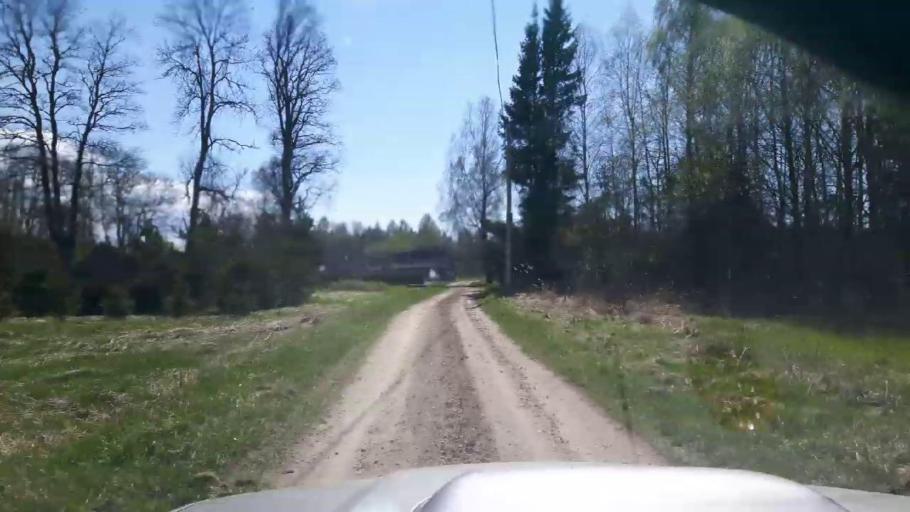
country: EE
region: Paernumaa
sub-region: Tootsi vald
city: Tootsi
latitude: 58.4631
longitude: 24.7982
